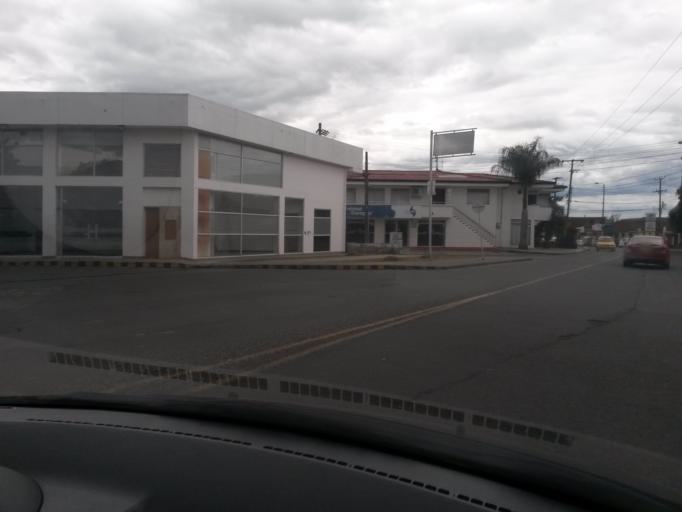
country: CO
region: Cauca
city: Popayan
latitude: 2.4558
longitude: -76.5975
